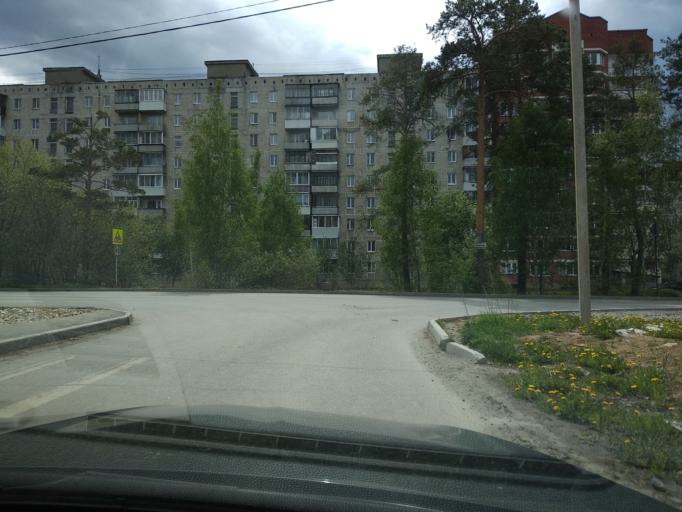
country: RU
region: Sverdlovsk
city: Beryozovsky
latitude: 56.9137
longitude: 60.8178
